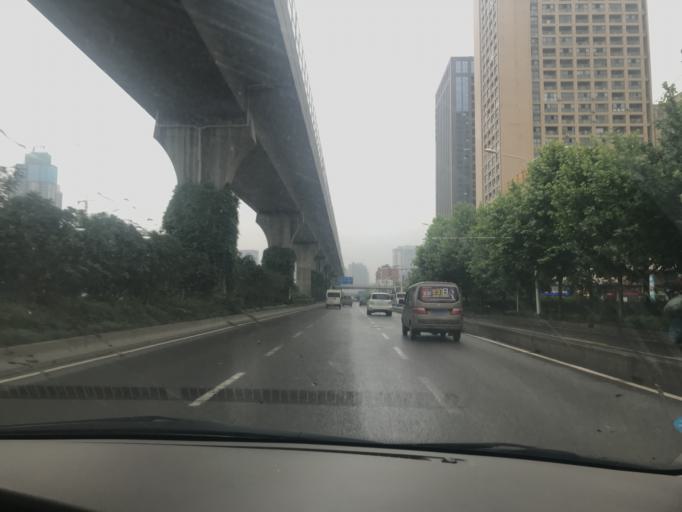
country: CN
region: Hubei
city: Jiang'an
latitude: 30.6255
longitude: 114.3118
